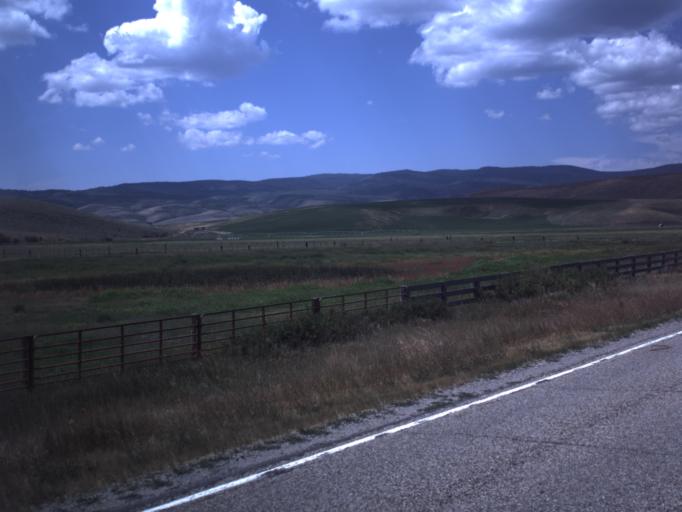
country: US
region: Utah
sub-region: Rich County
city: Randolph
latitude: 41.8414
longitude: -111.3448
